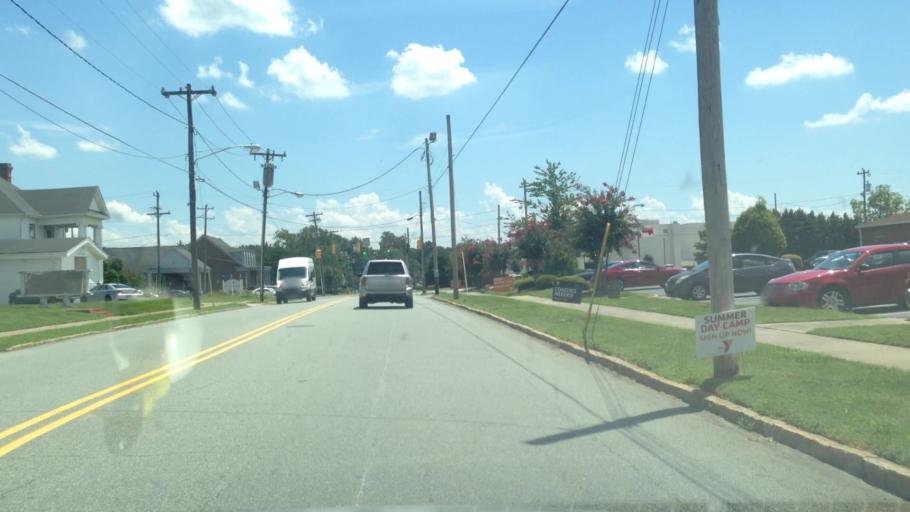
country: US
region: North Carolina
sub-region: Rockingham County
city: Reidsville
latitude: 36.3560
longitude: -79.6662
